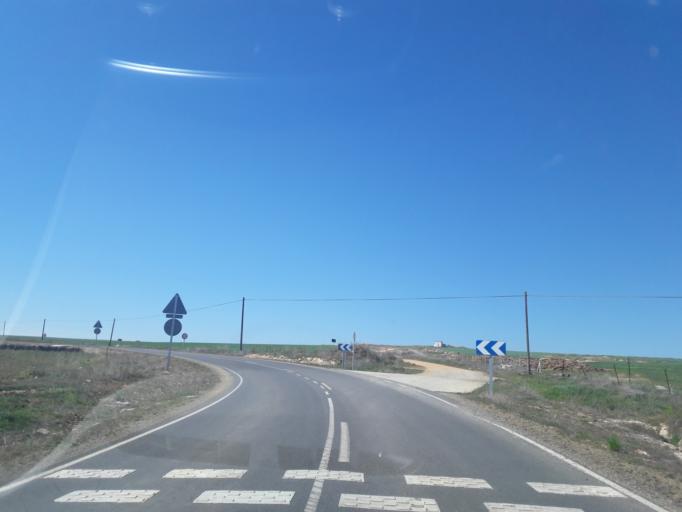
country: ES
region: Castille and Leon
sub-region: Provincia de Salamanca
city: Valdemierque
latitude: 40.8206
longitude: -5.5849
